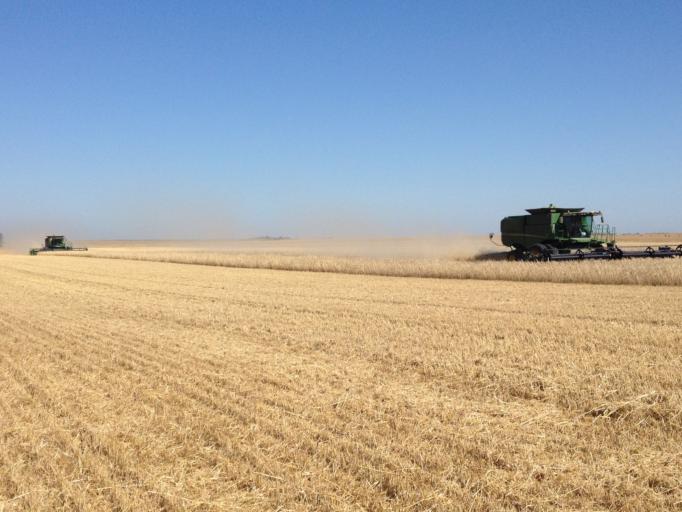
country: US
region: North Dakota
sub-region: McLean County
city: Garrison
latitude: 47.7180
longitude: -101.7618
